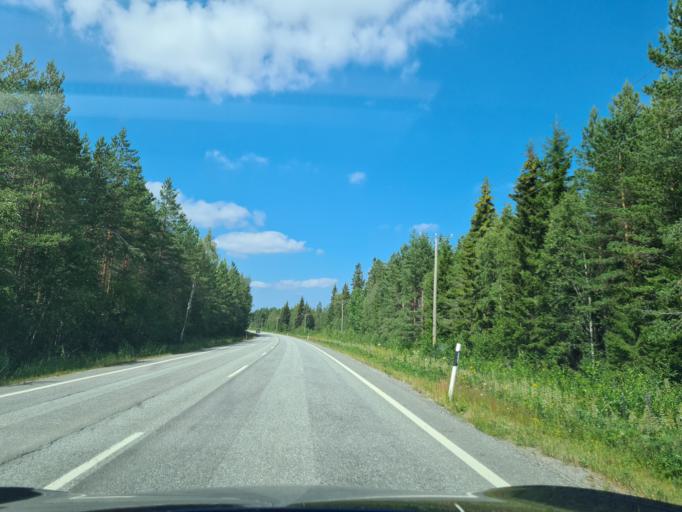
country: FI
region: Ostrobothnia
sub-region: Vaasa
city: Vaasa
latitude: 63.1771
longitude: 21.5765
